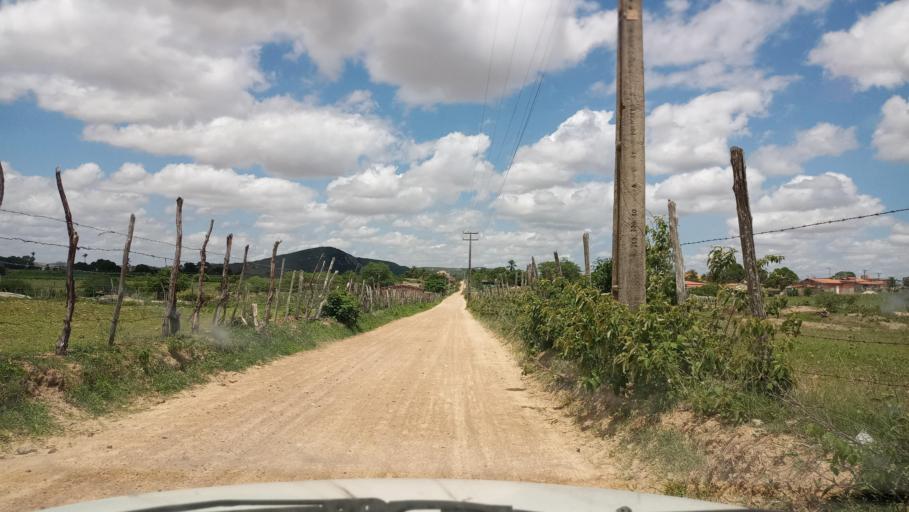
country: BR
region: Rio Grande do Norte
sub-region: Sao Jose Do Campestre
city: Sao Jose do Campestre
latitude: -6.4414
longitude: -35.6308
